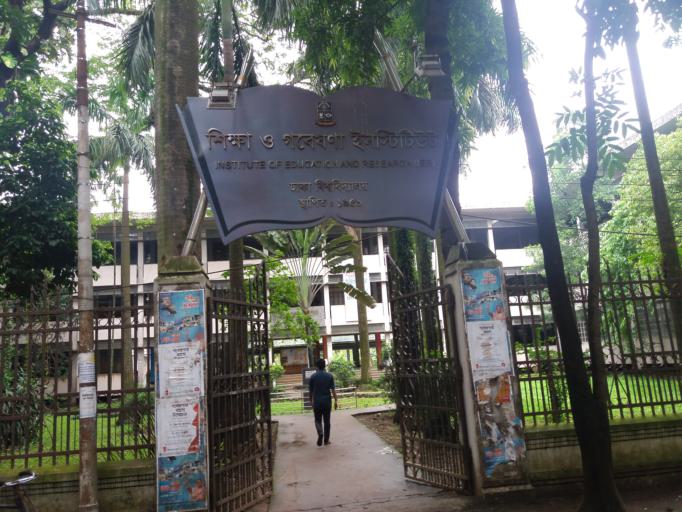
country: BD
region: Dhaka
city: Azimpur
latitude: 23.7340
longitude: 90.3909
